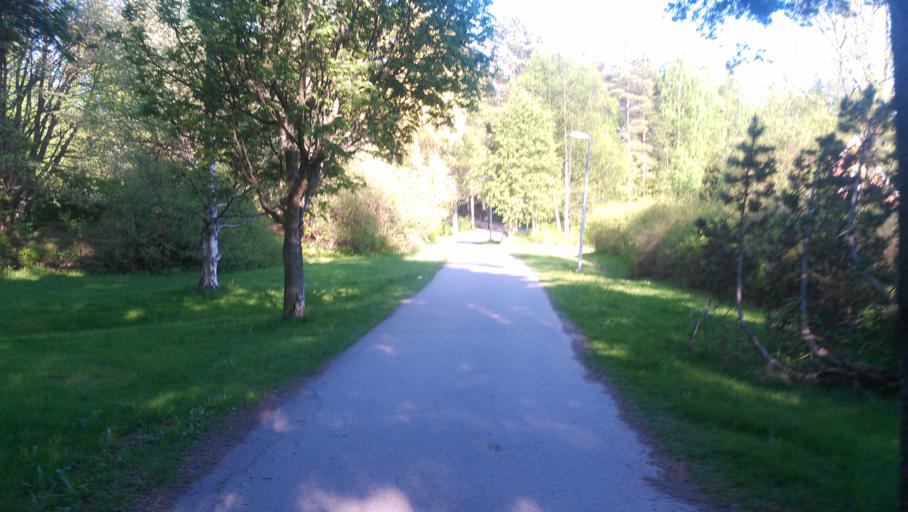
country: SE
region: Vaesterbotten
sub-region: Umea Kommun
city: Umea
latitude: 63.8125
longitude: 20.3003
